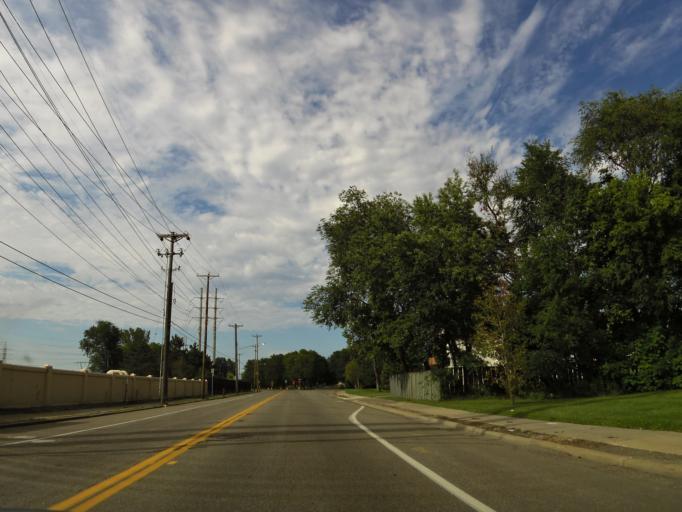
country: US
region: Minnesota
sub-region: Anoka County
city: Columbia Heights
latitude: 45.0207
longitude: -93.2727
